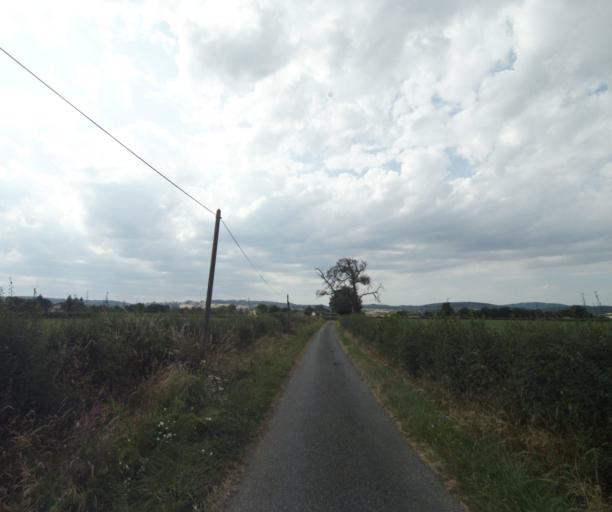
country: FR
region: Bourgogne
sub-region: Departement de Saone-et-Loire
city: Gueugnon
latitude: 46.6115
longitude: 4.0815
